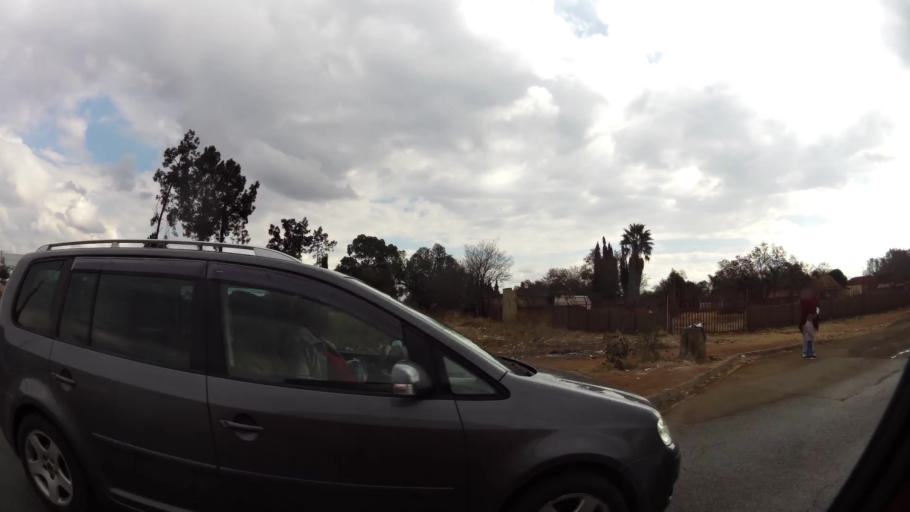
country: ZA
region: Gauteng
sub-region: Sedibeng District Municipality
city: Vanderbijlpark
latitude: -26.7067
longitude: 27.8243
